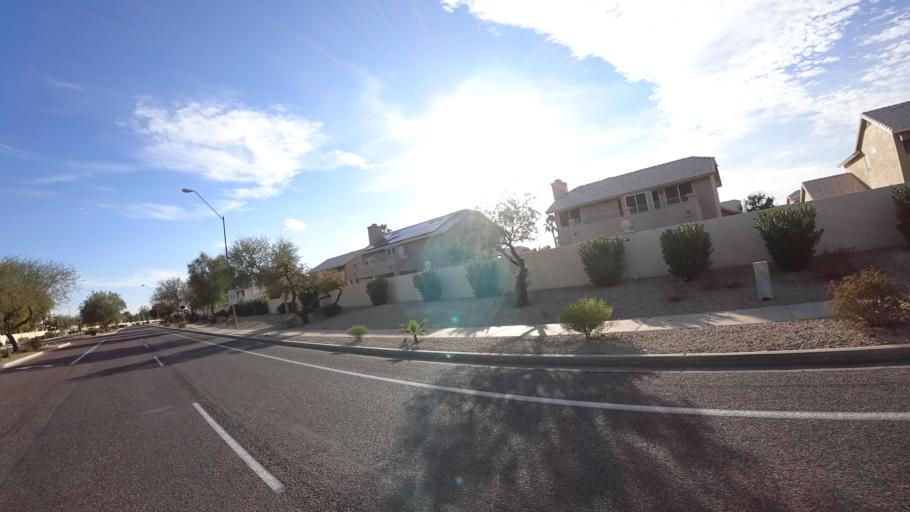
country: US
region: Arizona
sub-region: Maricopa County
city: Sun City
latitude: 33.6148
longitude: -112.2536
